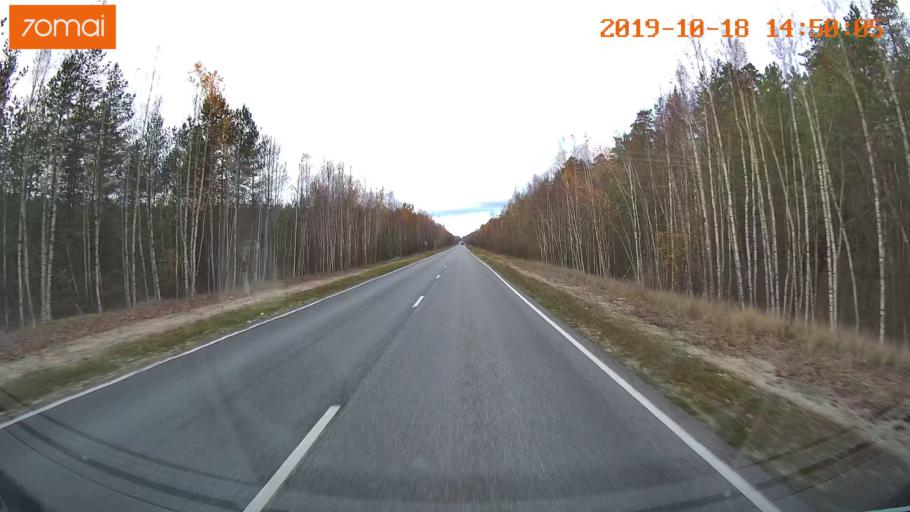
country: RU
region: Vladimir
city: Kurlovo
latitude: 55.4225
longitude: 40.6465
